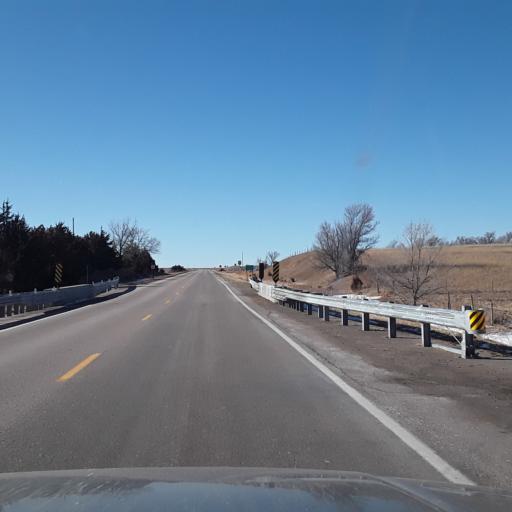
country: US
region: Nebraska
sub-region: Dawson County
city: Gothenburg
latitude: 40.7058
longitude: -100.2199
